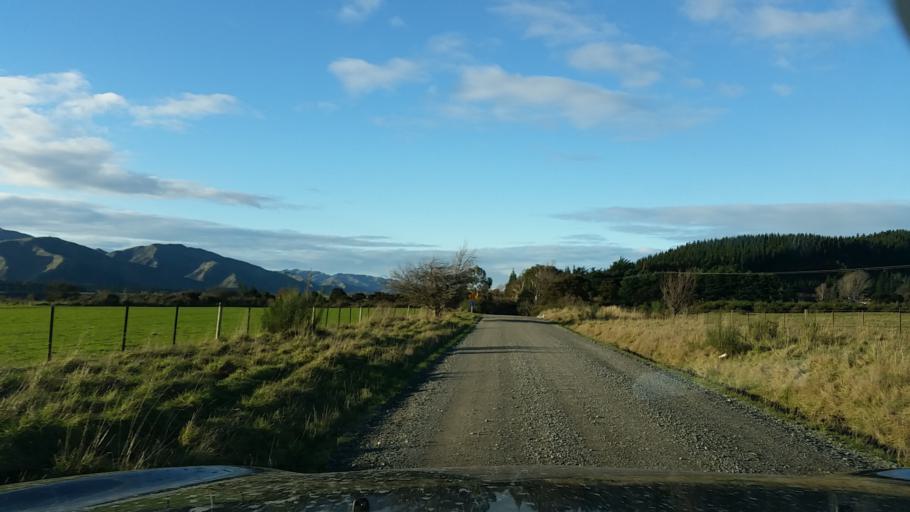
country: NZ
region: Marlborough
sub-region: Marlborough District
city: Blenheim
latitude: -41.7332
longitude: 173.8923
